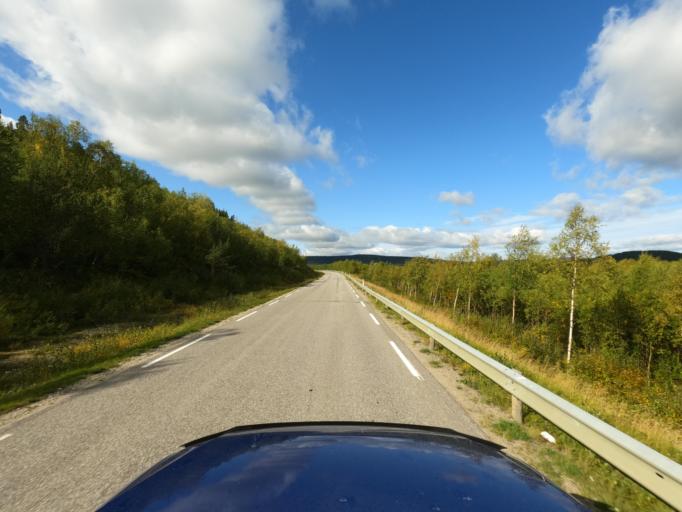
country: NO
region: Finnmark Fylke
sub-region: Karasjok
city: Karasjohka
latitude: 69.4562
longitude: 25.5635
